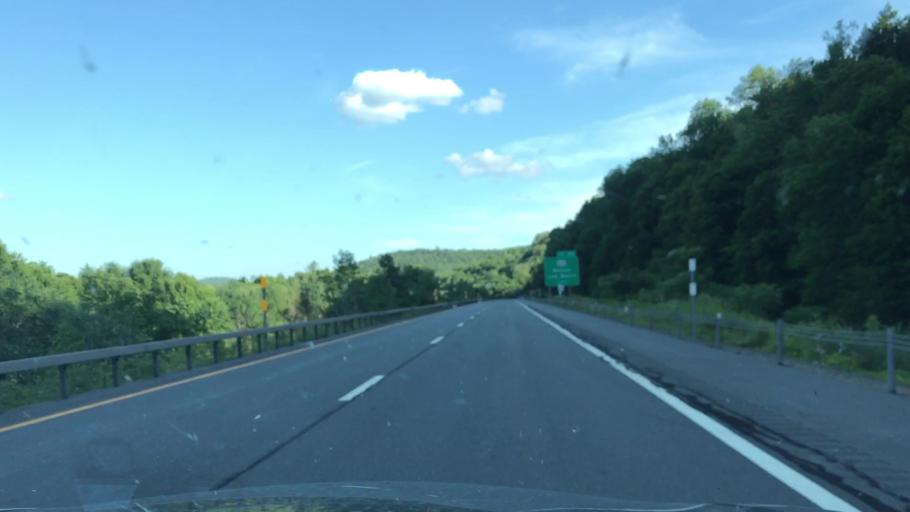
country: US
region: New York
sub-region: Sullivan County
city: Livingston Manor
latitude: 41.9437
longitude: -74.9307
